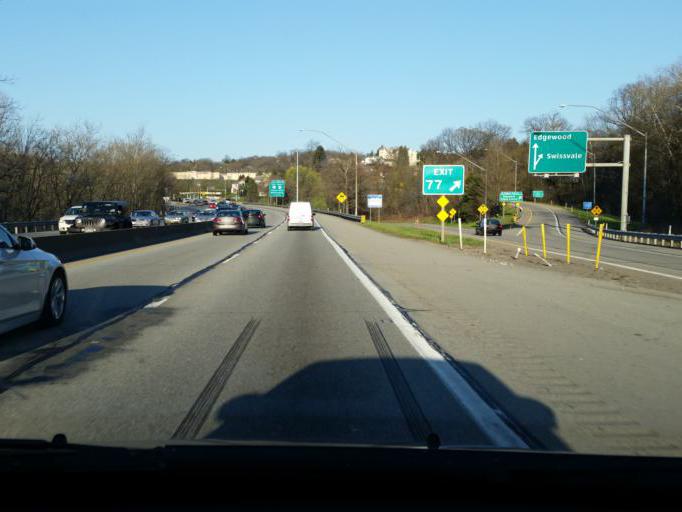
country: US
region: Pennsylvania
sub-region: Allegheny County
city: Swissvale
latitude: 40.4260
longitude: -79.8961
